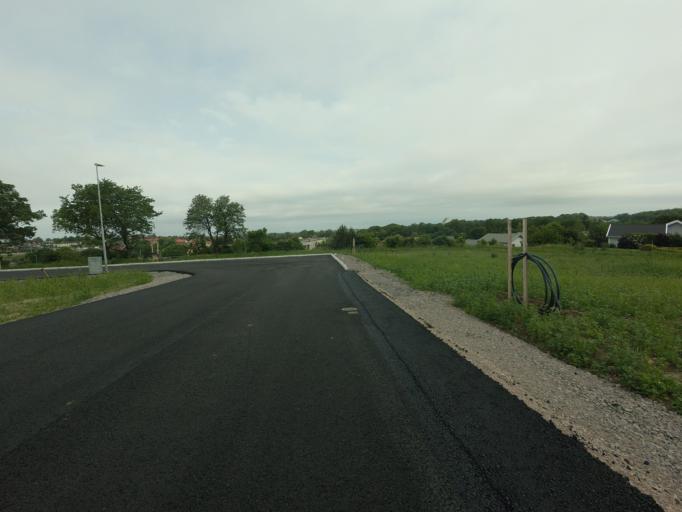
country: SE
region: Skane
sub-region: Bastads Kommun
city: Forslov
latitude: 56.3499
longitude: 12.8250
